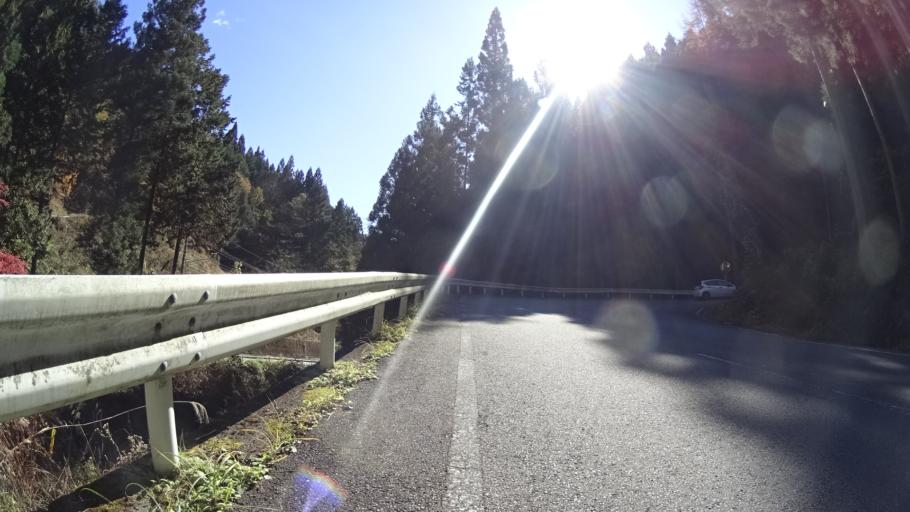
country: JP
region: Yamanashi
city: Otsuki
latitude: 35.7661
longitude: 138.9353
